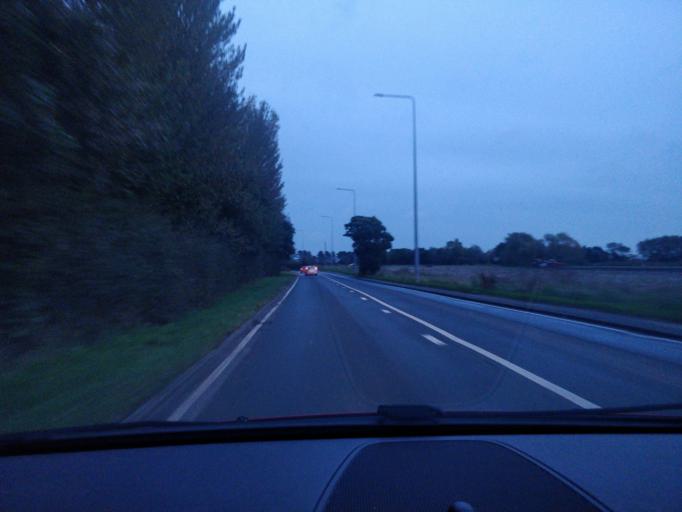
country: GB
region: England
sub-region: Lancashire
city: Ormskirk
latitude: 53.5868
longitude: -2.9135
